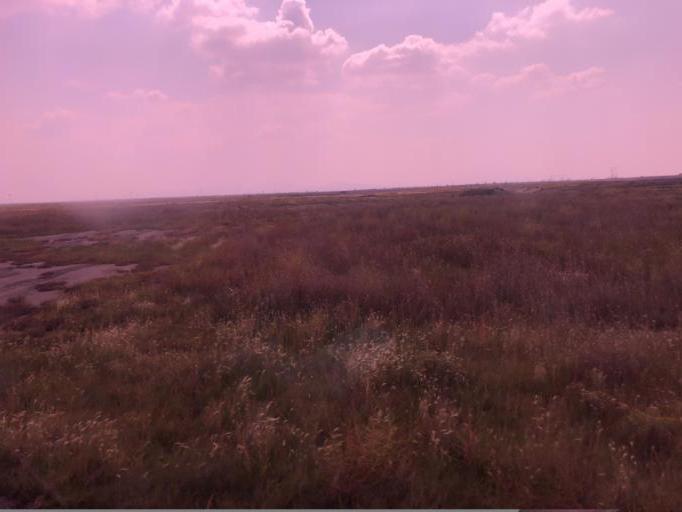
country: MX
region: Mexico
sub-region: Atenco
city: Colonia el Salado
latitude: 19.5519
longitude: -98.9884
